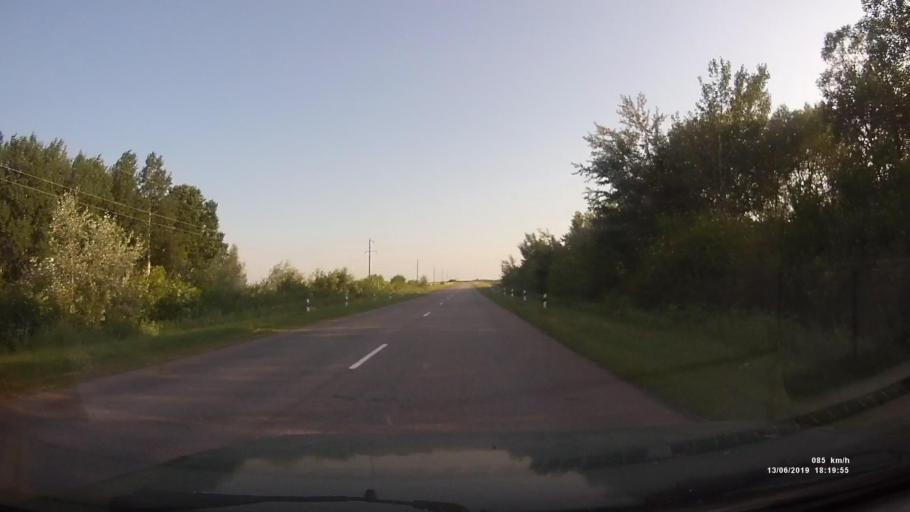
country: RU
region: Rostov
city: Kazanskaya
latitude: 49.8903
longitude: 41.3030
